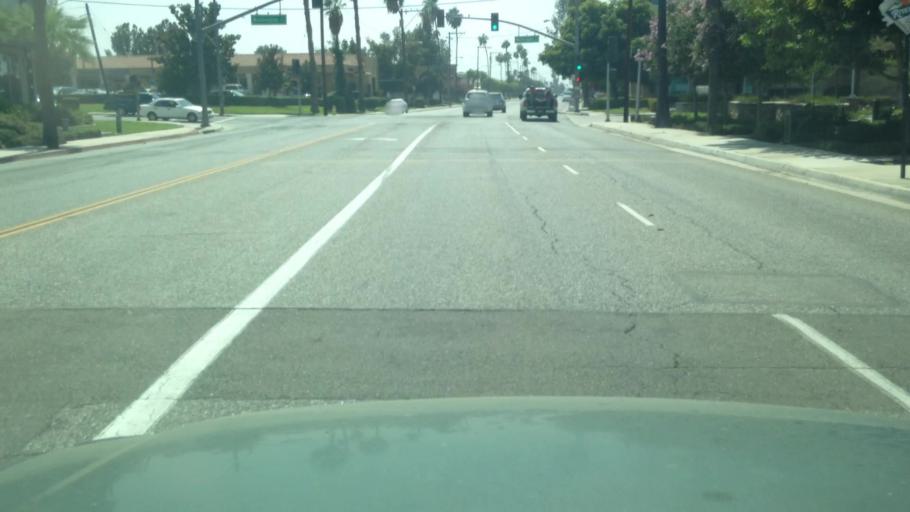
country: US
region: California
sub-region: Riverside County
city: Riverside
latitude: 33.9398
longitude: -117.3964
